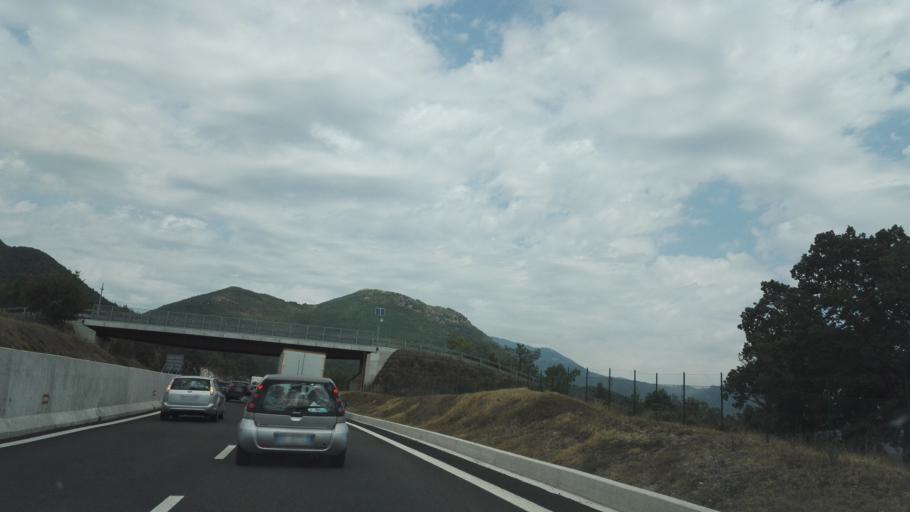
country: IT
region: Calabria
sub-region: Provincia di Cosenza
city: Laino Borgo
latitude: 39.9746
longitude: 15.9363
